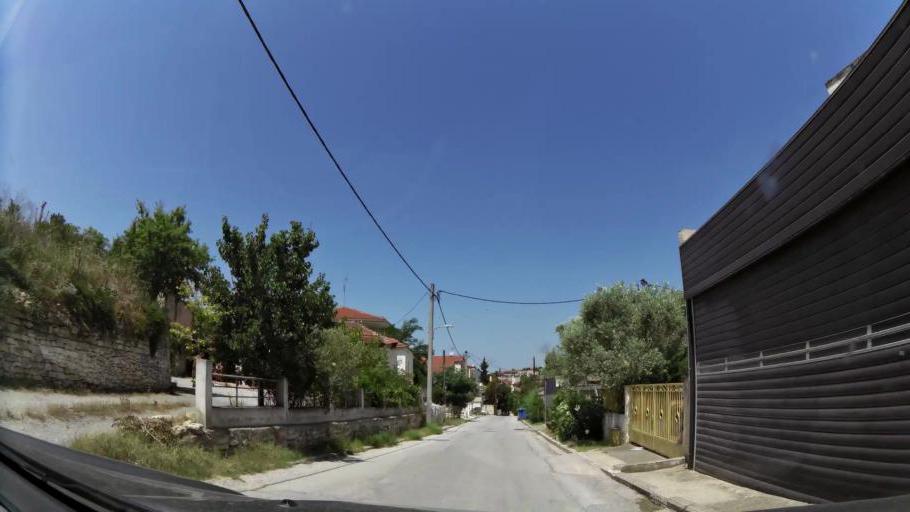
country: GR
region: Central Macedonia
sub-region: Nomos Thessalonikis
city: Trilofos
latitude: 40.4648
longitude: 22.9682
